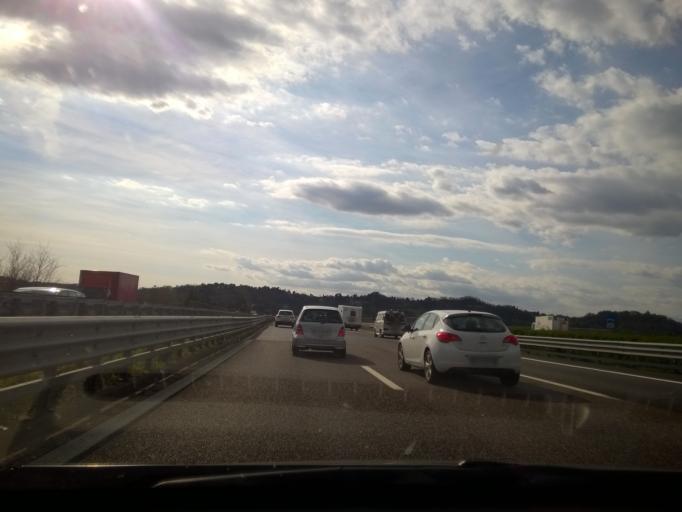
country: IT
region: Veneto
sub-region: Provincia di Vicenza
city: Arcugnano-Torri
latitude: 45.5170
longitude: 11.5779
